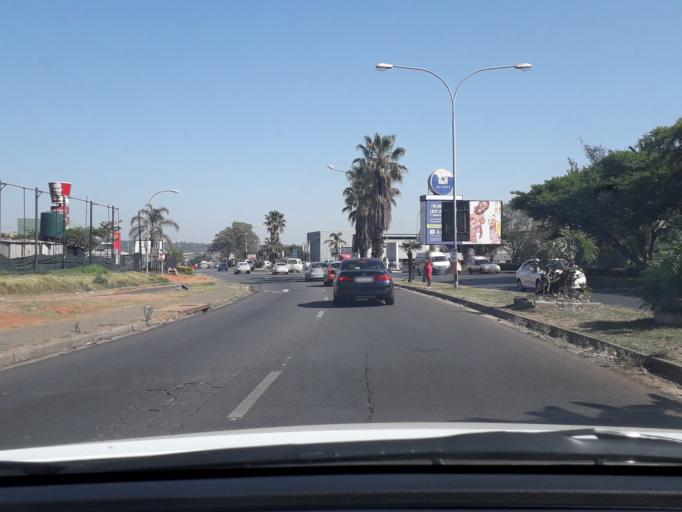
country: ZA
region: Gauteng
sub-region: City of Johannesburg Metropolitan Municipality
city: Johannesburg
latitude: -26.1305
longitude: 27.9719
